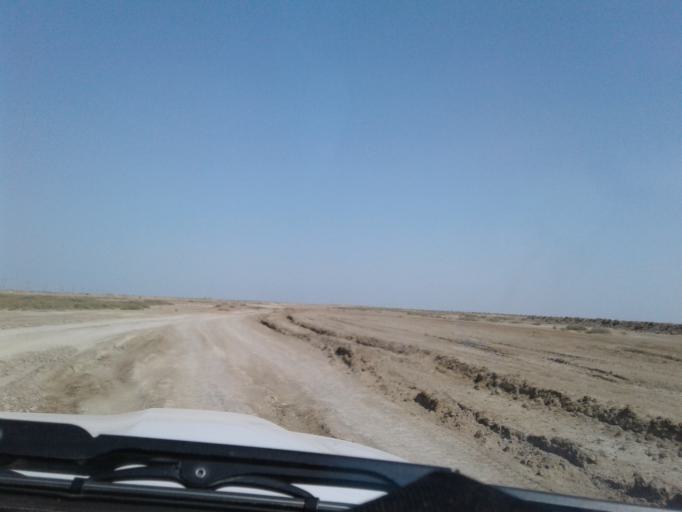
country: IR
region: Golestan
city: Gomishan
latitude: 37.8213
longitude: 53.9222
